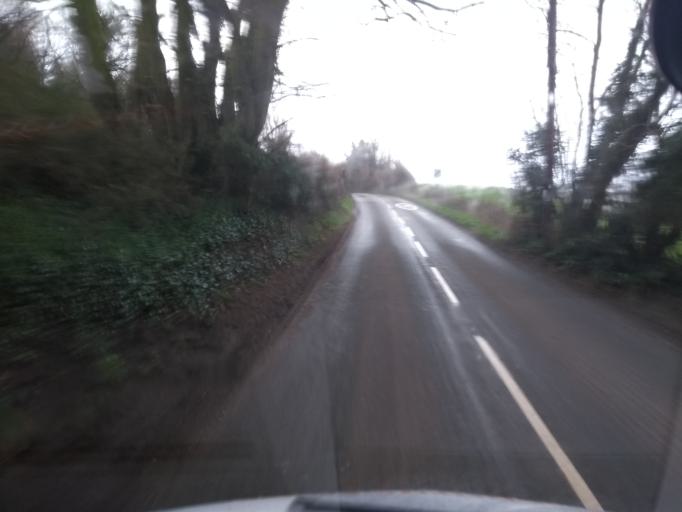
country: GB
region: England
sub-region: Somerset
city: Bruton
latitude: 51.0973
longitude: -2.4664
